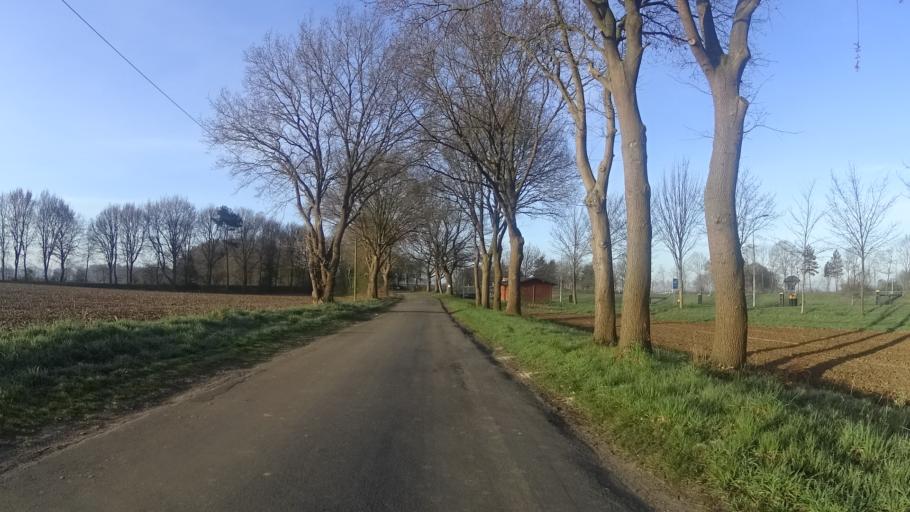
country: DE
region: Lower Saxony
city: Fresenburg
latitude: 52.9056
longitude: 7.3126
